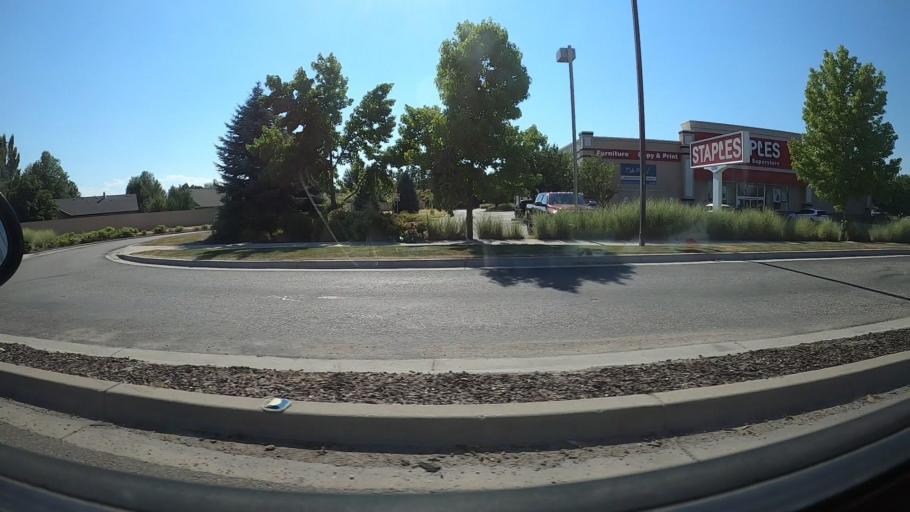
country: US
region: Idaho
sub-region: Ada County
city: Eagle
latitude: 43.6623
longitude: -116.3549
